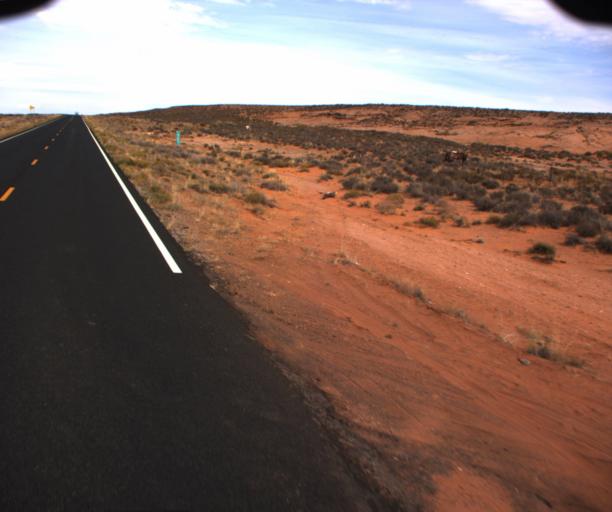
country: US
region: Arizona
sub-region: Apache County
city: Many Farms
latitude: 36.8784
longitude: -109.6299
